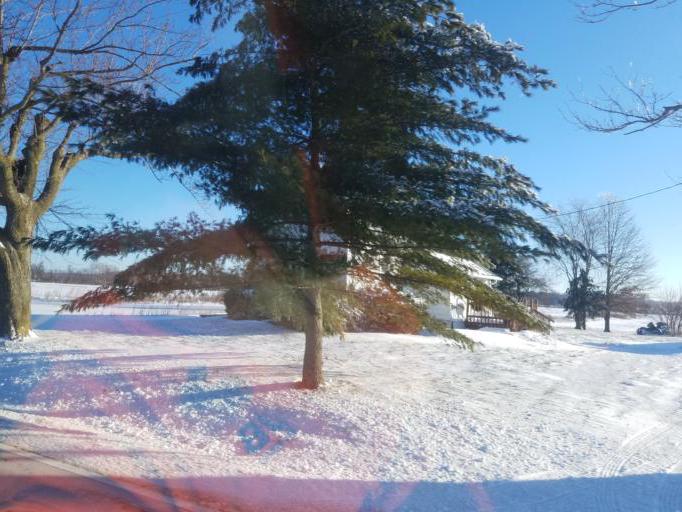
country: US
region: Ohio
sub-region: Delaware County
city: Sunbury
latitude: 40.3164
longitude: -82.9144
